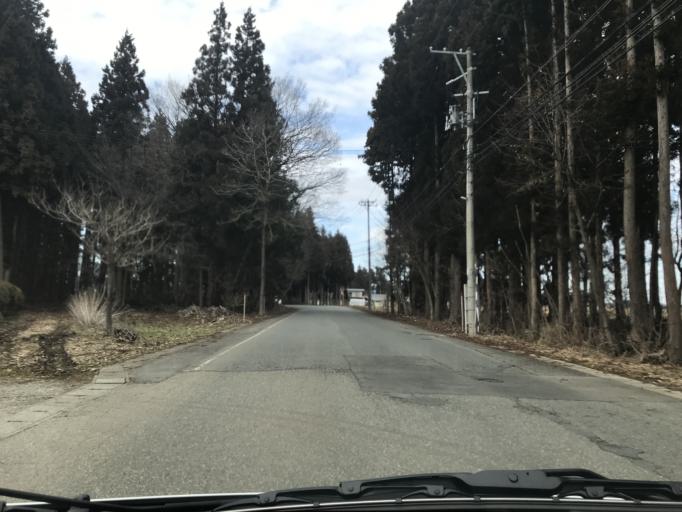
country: JP
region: Iwate
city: Kitakami
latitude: 39.3198
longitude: 140.9864
